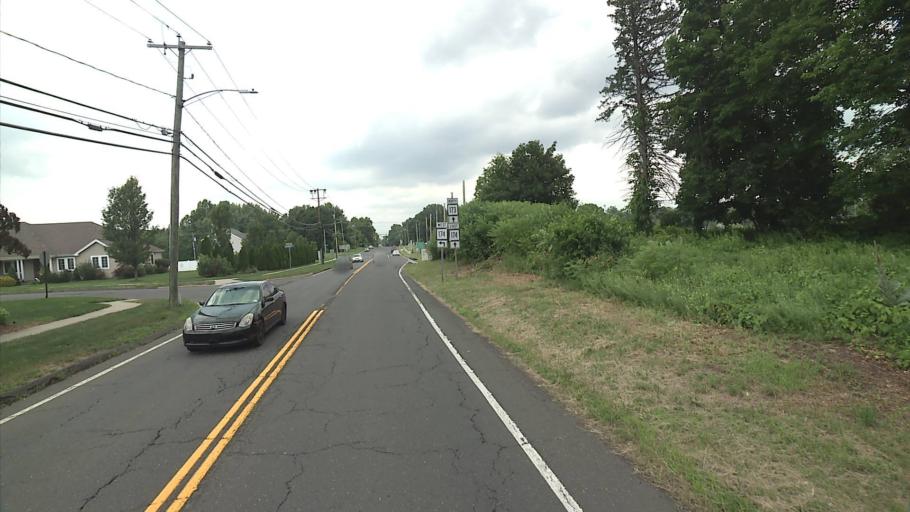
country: US
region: Connecticut
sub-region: Hartford County
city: Newington
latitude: 41.6741
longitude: -72.7289
